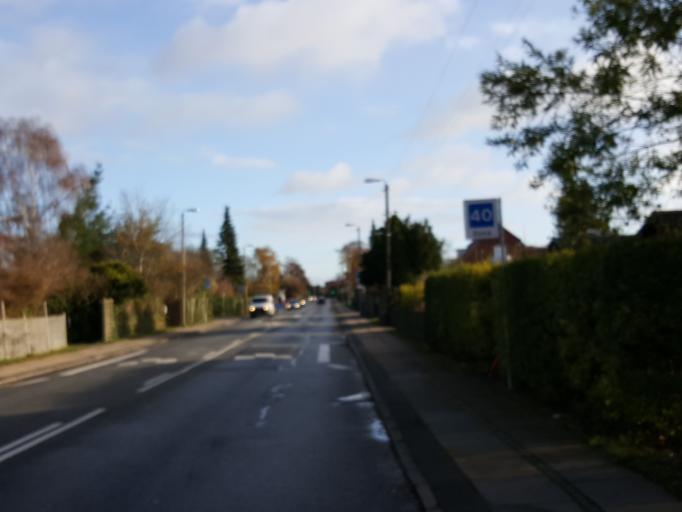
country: DK
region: Capital Region
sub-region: Tarnby Kommune
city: Tarnby
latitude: 55.6426
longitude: 12.6012
